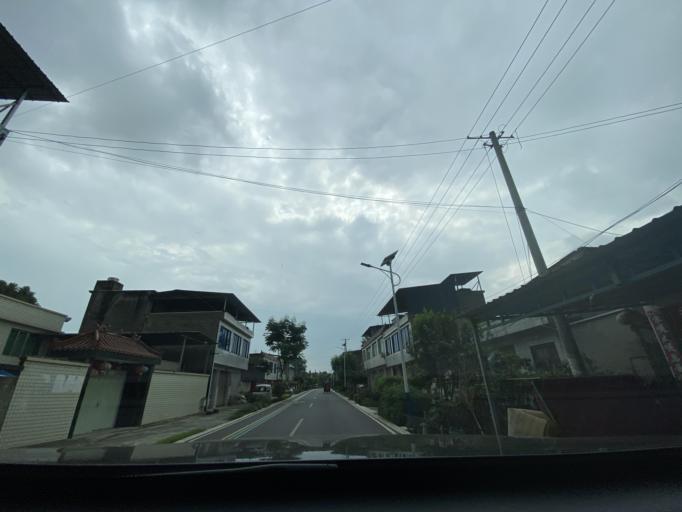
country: CN
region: Sichuan
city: Wujin
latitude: 30.4031
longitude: 103.9872
